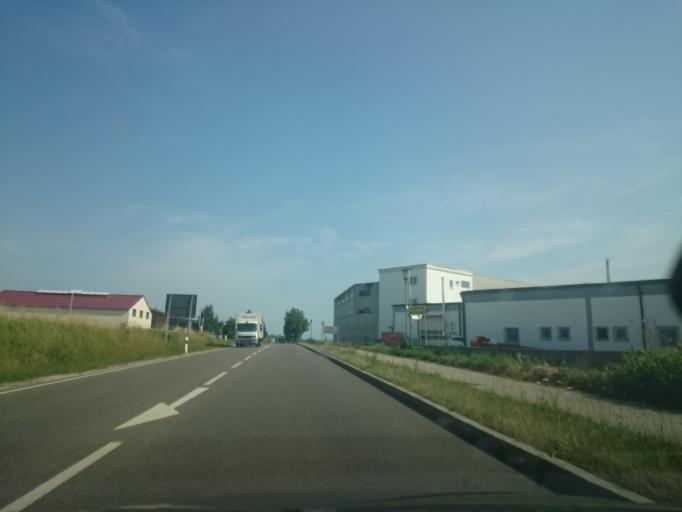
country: DE
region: Bavaria
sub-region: Swabia
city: Merching
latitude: 48.2482
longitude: 10.9907
